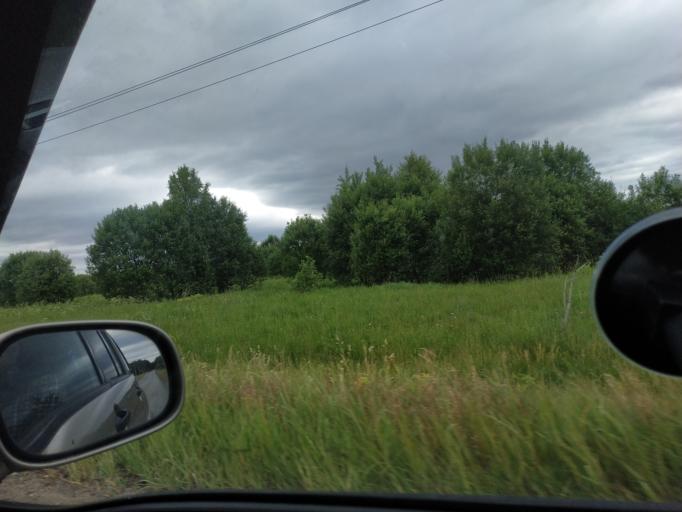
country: RU
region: Moskovskaya
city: Krasnoarmeysk
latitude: 56.0813
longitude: 38.2393
